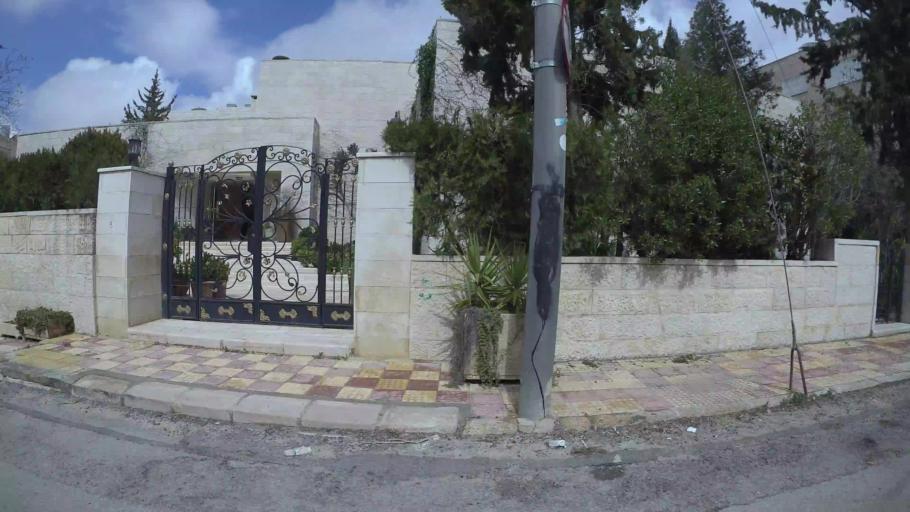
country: JO
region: Amman
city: Al Jubayhah
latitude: 31.9909
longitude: 35.8478
